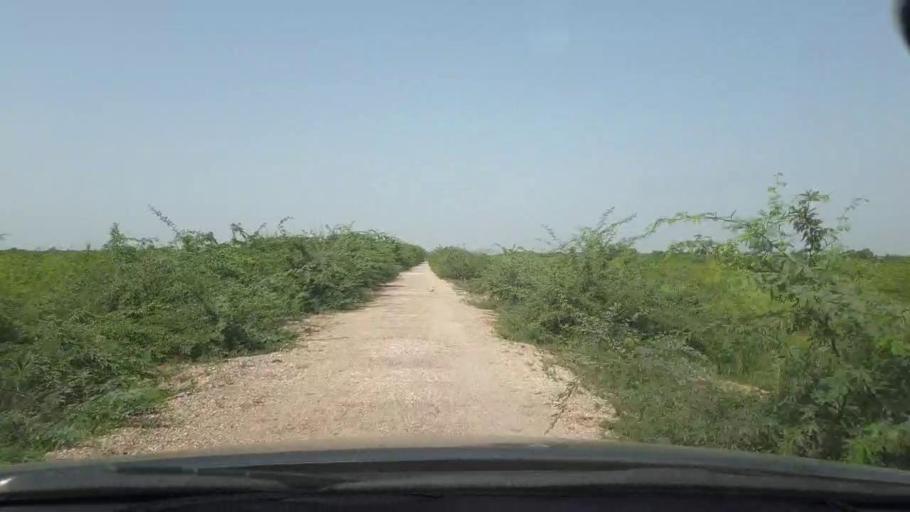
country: PK
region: Sindh
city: Naukot
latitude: 24.8099
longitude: 69.2719
